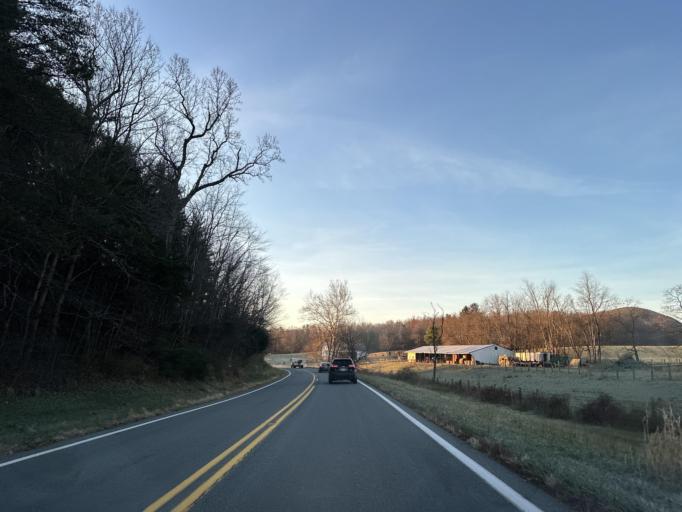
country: US
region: Virginia
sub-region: City of Staunton
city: Staunton
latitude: 38.2009
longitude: -79.2192
